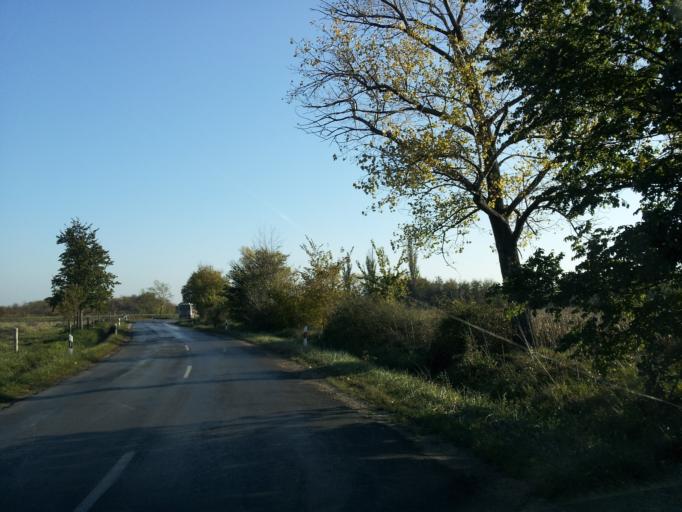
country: HU
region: Fejer
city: Fehervarcsurgo
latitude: 47.3025
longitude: 18.2559
